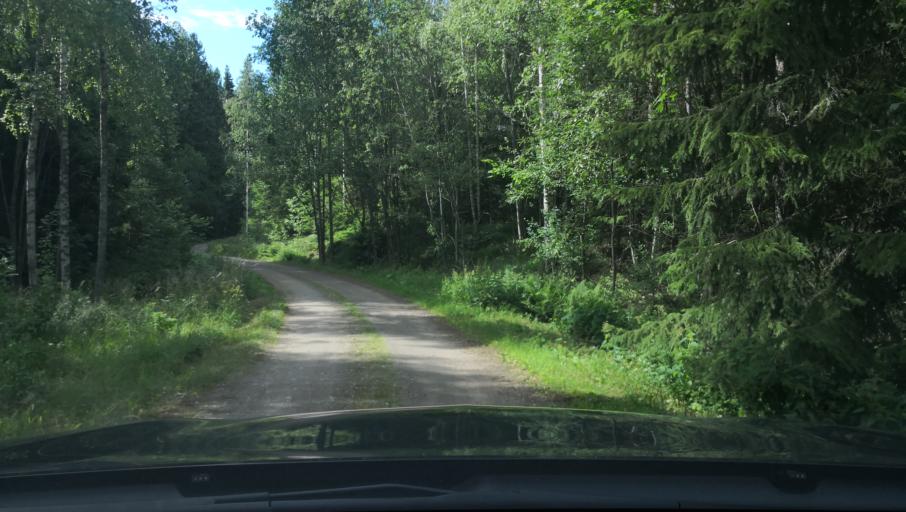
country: SE
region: Vaestmanland
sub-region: Kopings Kommun
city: Koping
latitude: 59.6403
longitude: 16.0661
